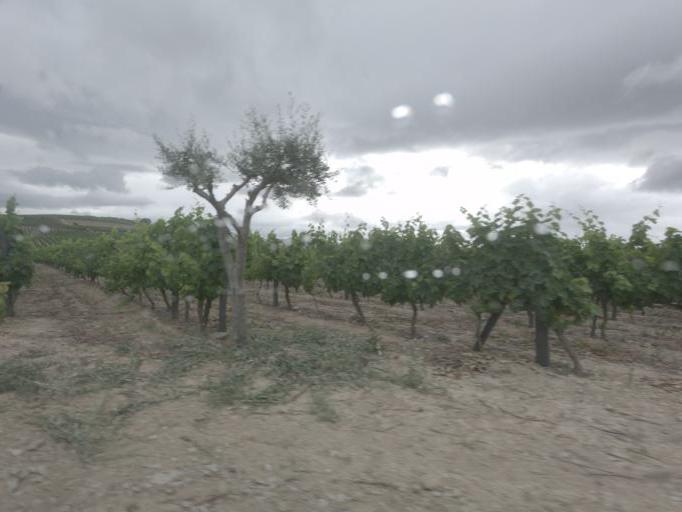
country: PT
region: Vila Real
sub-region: Sabrosa
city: Sabrosa
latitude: 41.2427
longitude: -7.4972
